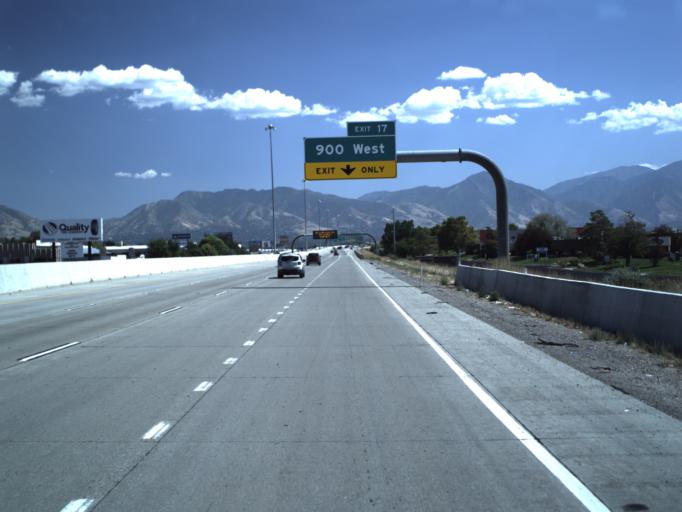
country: US
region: Utah
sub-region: Salt Lake County
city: South Salt Lake
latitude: 40.7241
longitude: -111.9316
